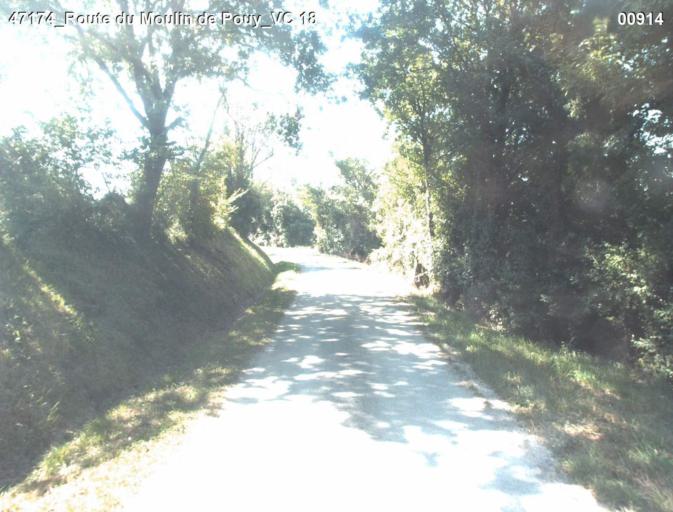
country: FR
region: Aquitaine
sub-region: Departement du Lot-et-Garonne
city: Mezin
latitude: 44.0561
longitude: 0.3184
